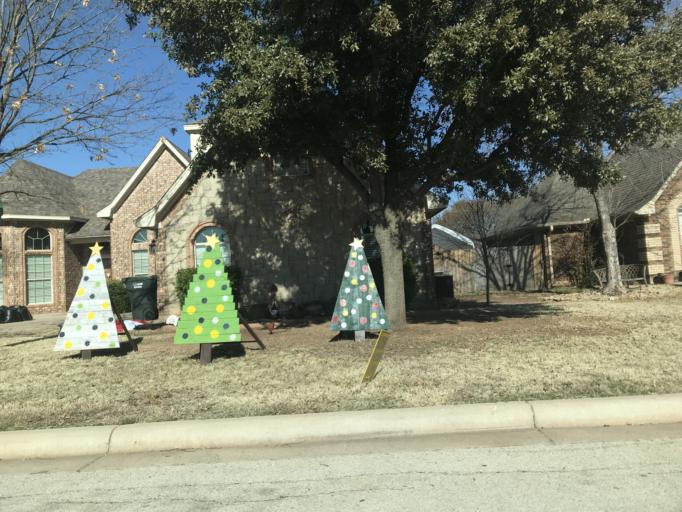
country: US
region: Texas
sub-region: Taylor County
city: Abilene
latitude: 32.3819
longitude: -99.7671
